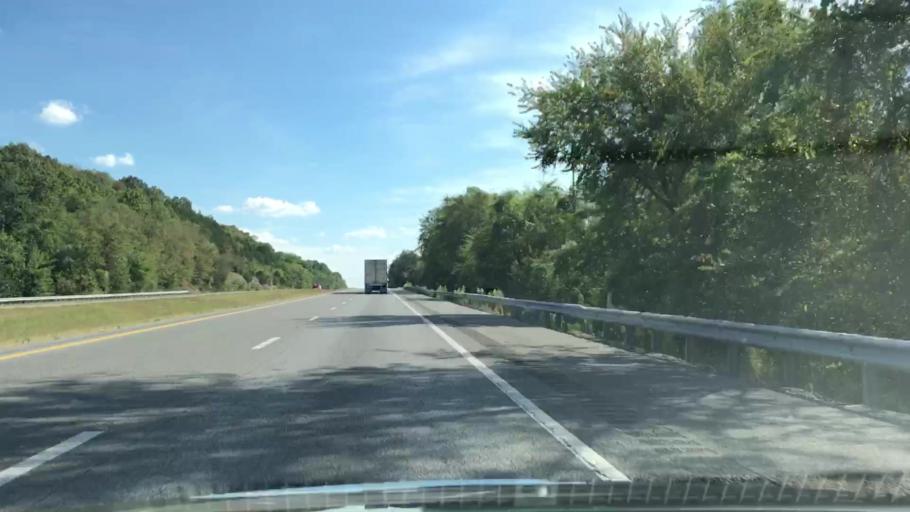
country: US
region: Alabama
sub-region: Limestone County
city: Ardmore
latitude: 35.0287
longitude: -86.8791
